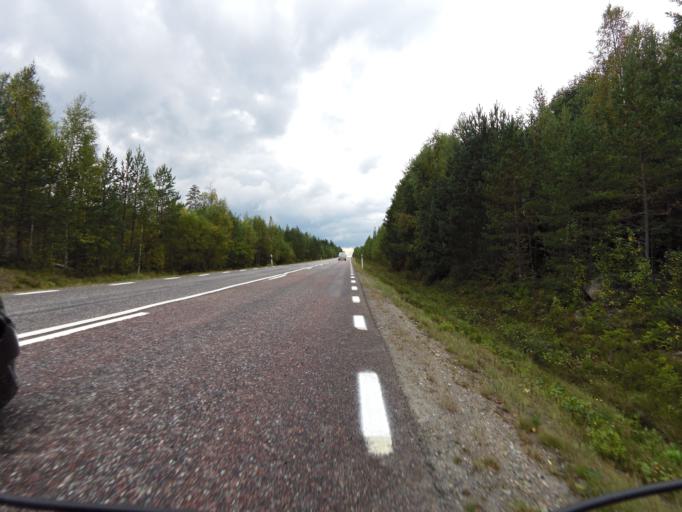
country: SE
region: Gaevleborg
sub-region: Ockelbo Kommun
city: Ockelbo
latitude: 60.8896
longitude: 16.9121
